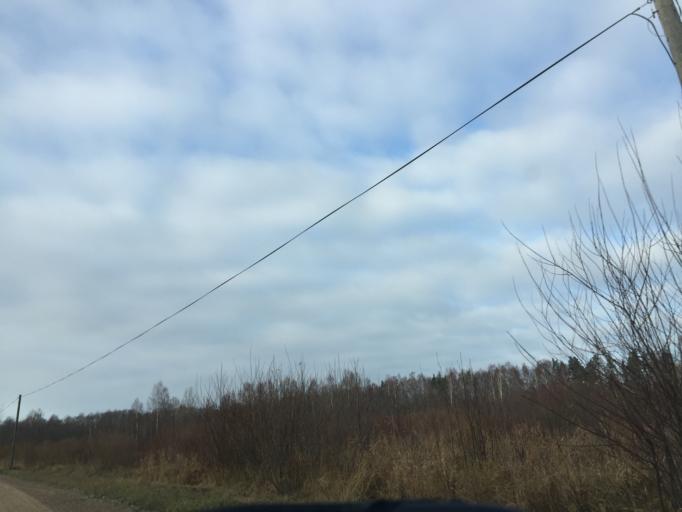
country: LV
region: Saulkrastu
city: Saulkrasti
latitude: 57.4666
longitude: 24.4056
